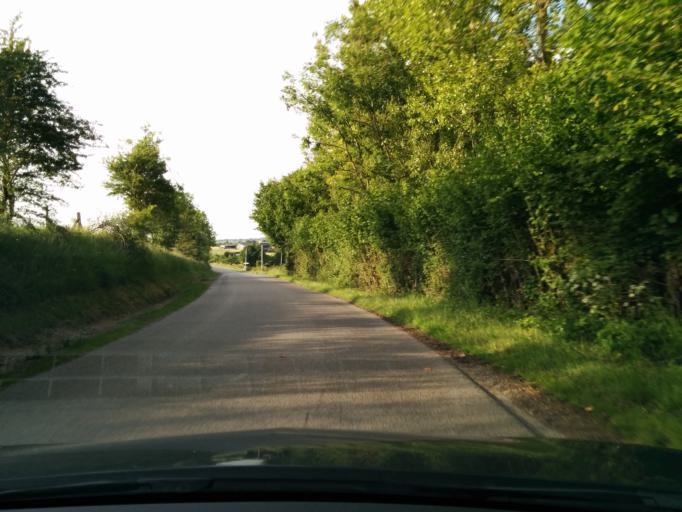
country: FR
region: Haute-Normandie
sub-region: Departement de la Seine-Maritime
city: La Feuillie
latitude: 49.5224
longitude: 1.4906
